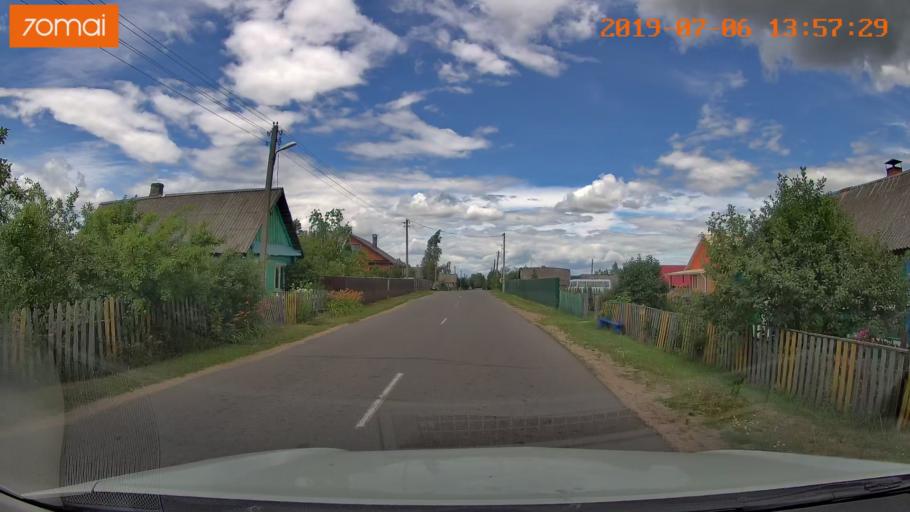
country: BY
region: Minsk
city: Ivyanyets
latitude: 53.7746
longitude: 26.8064
